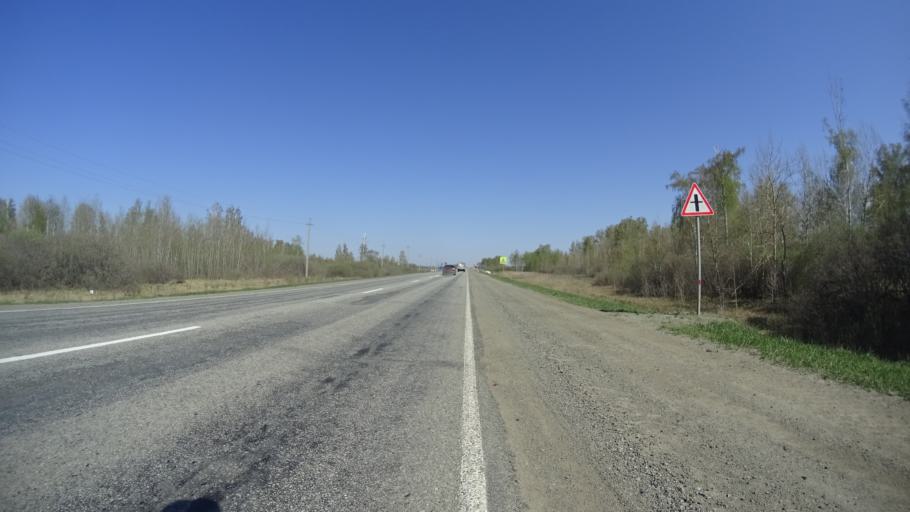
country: RU
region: Chelyabinsk
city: Troitsk
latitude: 54.1851
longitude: 61.4342
